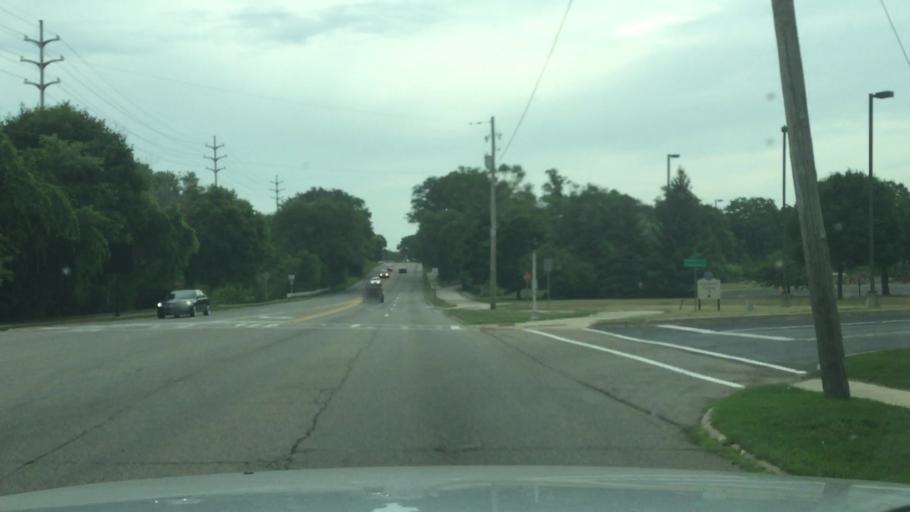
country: US
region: Michigan
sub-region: Genesee County
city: Flint
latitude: 43.0256
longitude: -83.6724
